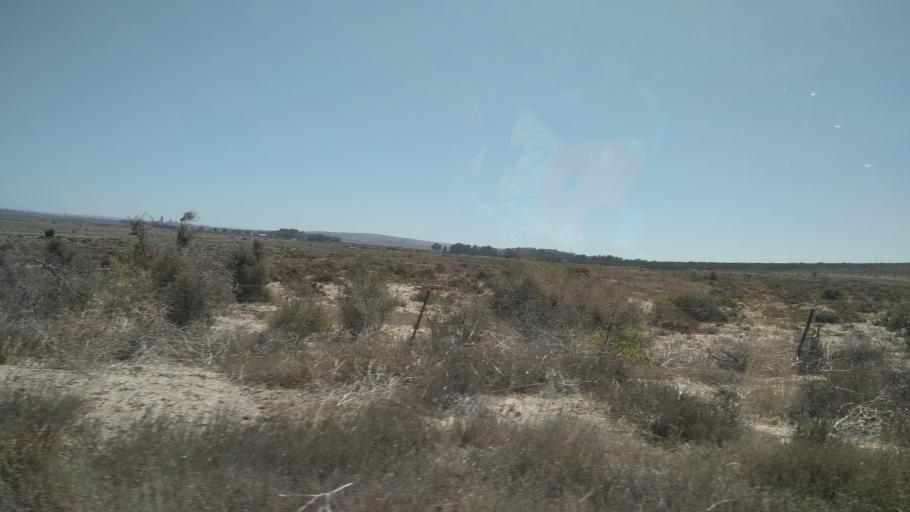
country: ZA
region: Western Cape
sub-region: West Coast District Municipality
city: Vredenburg
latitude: -33.0157
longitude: 18.1139
